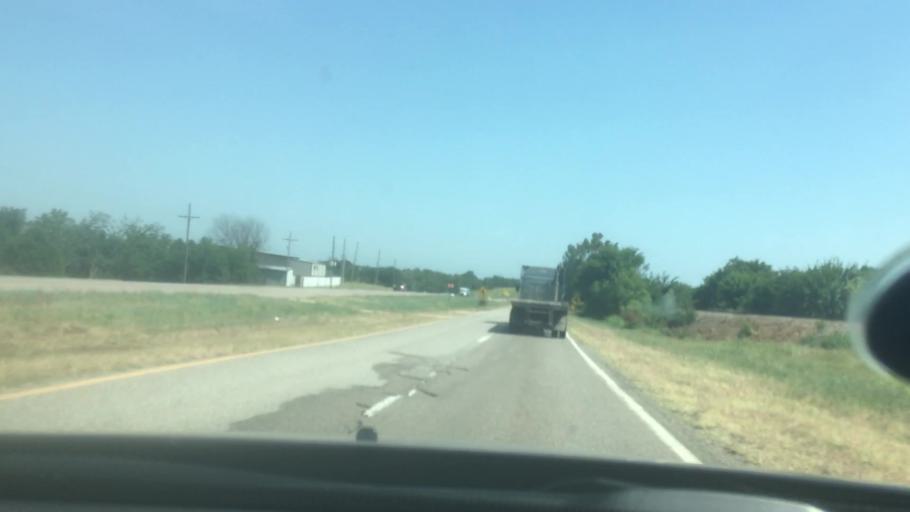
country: US
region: Oklahoma
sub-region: Pontotoc County
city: Ada
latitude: 34.7347
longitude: -96.7088
